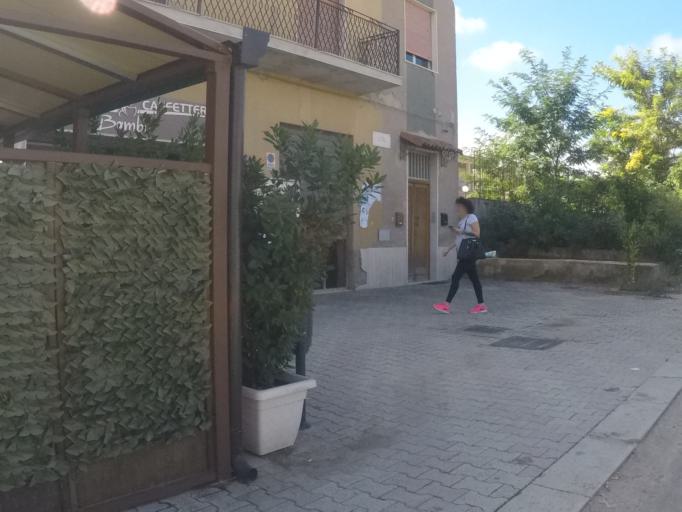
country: IT
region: Sicily
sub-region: Enna
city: Pietraperzia
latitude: 37.4161
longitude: 14.1330
